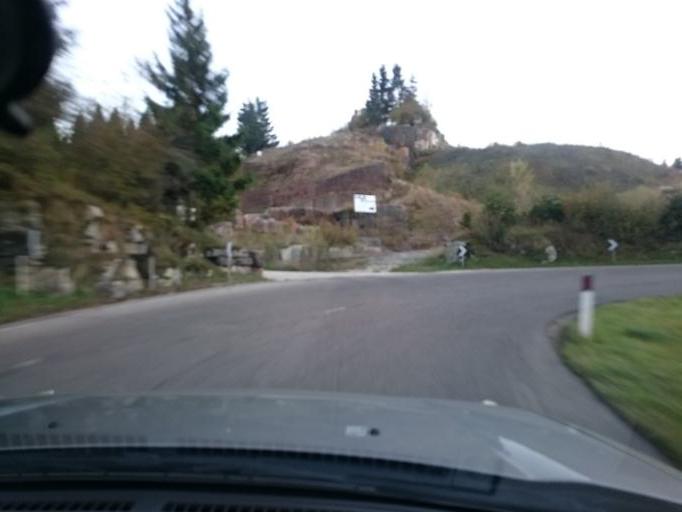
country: IT
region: Veneto
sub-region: Provincia di Vicenza
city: Canove di Roana
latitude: 45.8488
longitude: 11.4534
